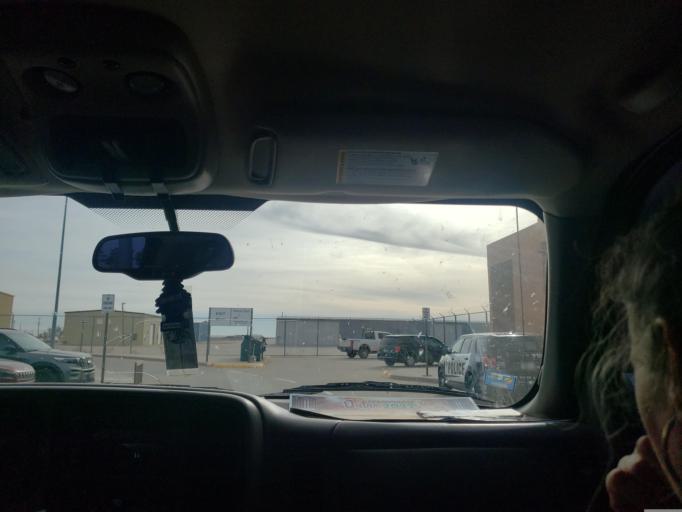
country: US
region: Kansas
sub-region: Finney County
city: Garden City
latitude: 37.9268
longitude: -100.7197
